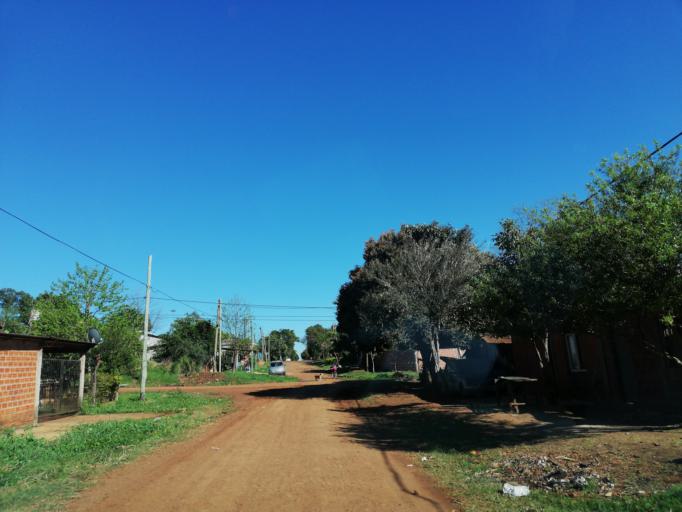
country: AR
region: Misiones
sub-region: Departamento de Capital
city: Posadas
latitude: -27.3954
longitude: -55.9305
